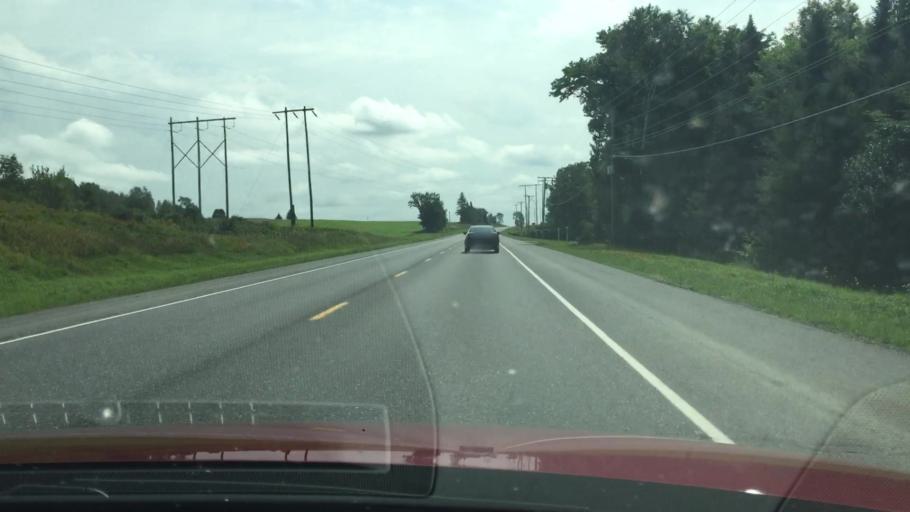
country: US
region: Maine
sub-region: Aroostook County
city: Easton
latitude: 46.4589
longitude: -67.8599
